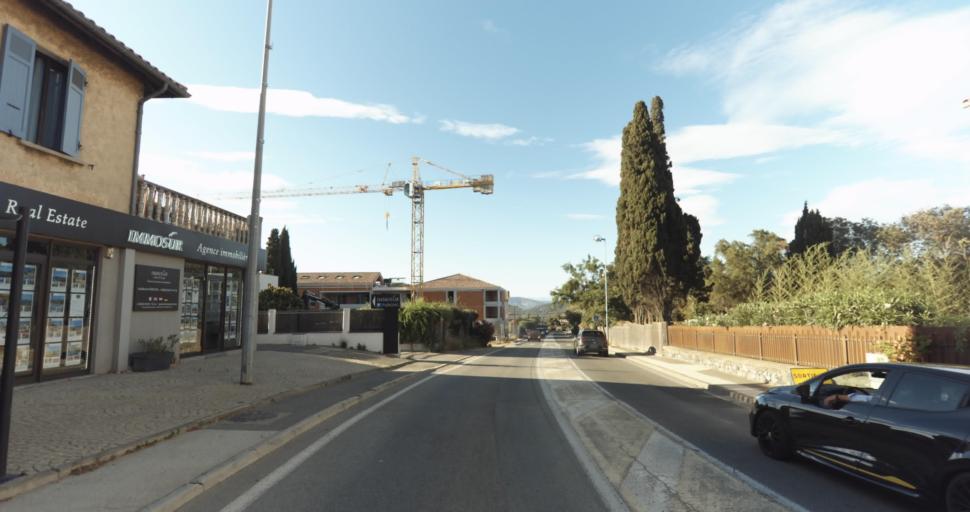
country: FR
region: Provence-Alpes-Cote d'Azur
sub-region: Departement du Var
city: La Croix-Valmer
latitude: 43.2098
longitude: 6.5685
